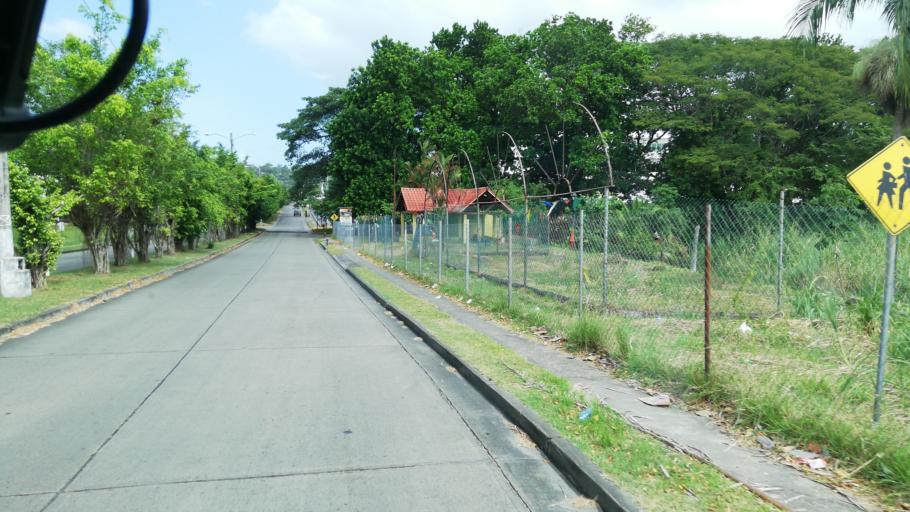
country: PA
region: Panama
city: San Miguelito
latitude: 9.0533
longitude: -79.4595
